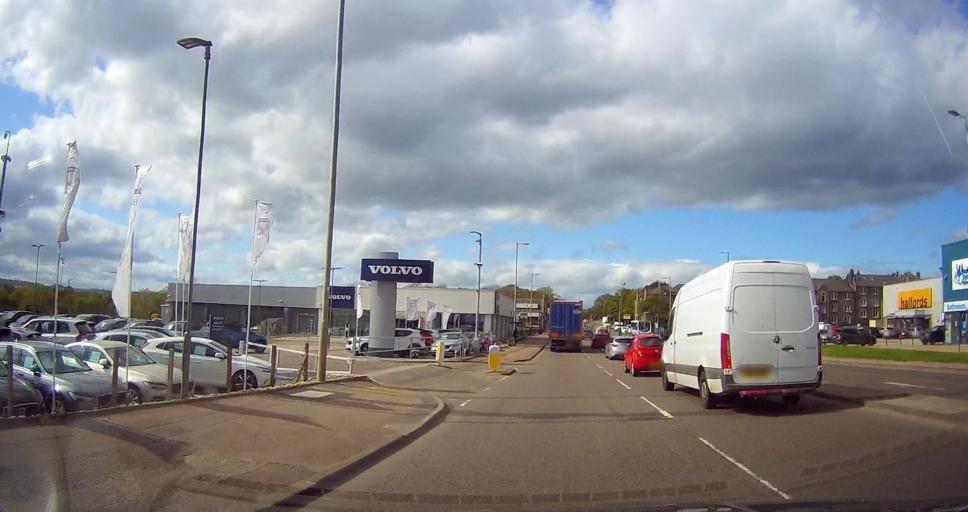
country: GB
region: Scotland
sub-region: Aberdeen City
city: Aberdeen
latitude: 57.1288
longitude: -2.0925
